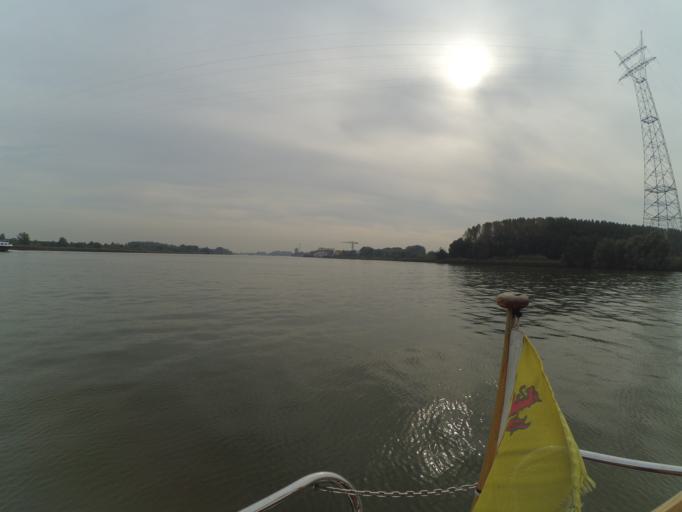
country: NL
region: South Holland
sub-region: Gemeente Ridderkerk
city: Ridderkerk
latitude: 51.8941
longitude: 4.5934
